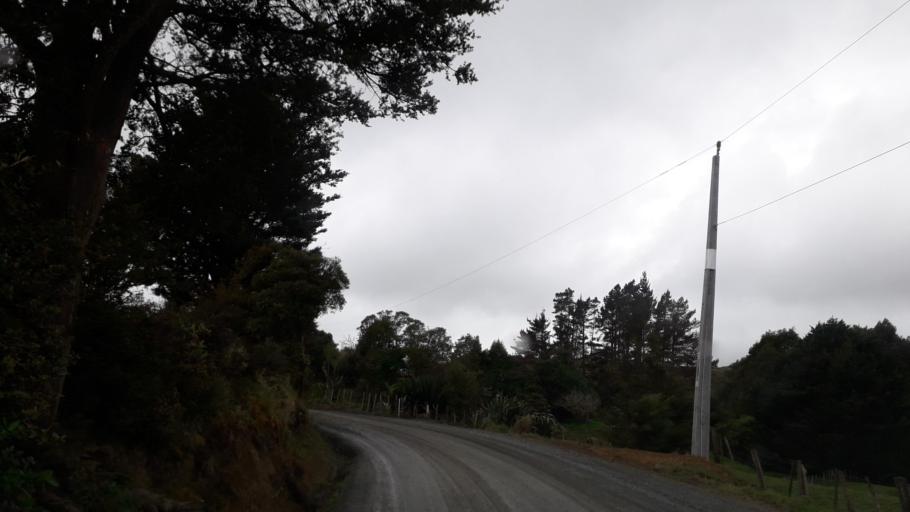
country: NZ
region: Northland
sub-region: Far North District
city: Kerikeri
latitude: -35.1260
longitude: 173.7449
